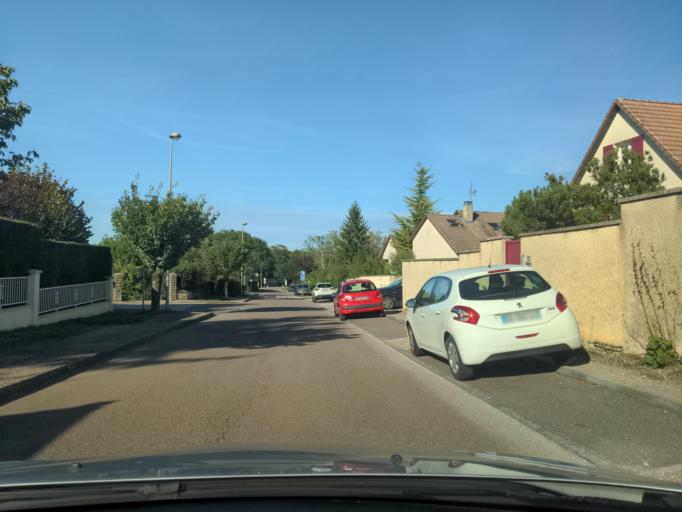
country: FR
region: Bourgogne
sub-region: Departement de la Cote-d'Or
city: Ruffey-les-Echirey
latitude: 47.3807
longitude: 5.0714
